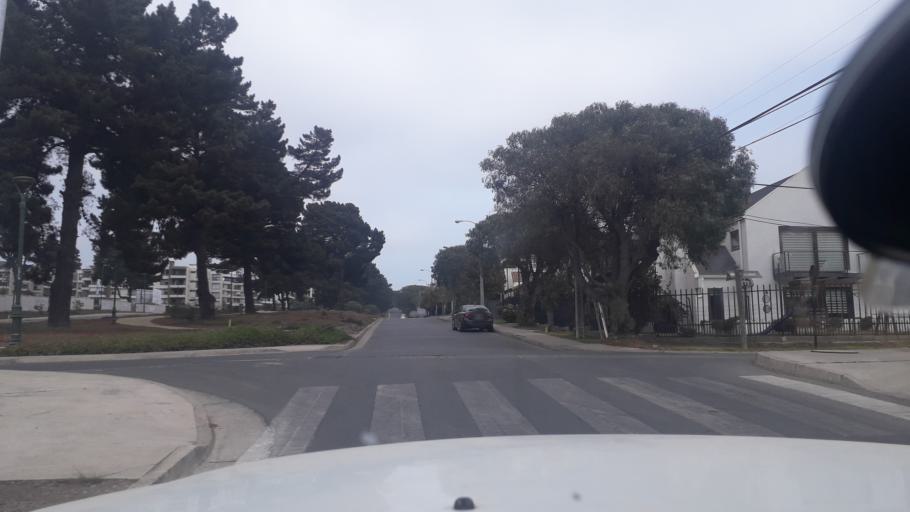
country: CL
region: Valparaiso
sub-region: Provincia de Valparaiso
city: Vina del Mar
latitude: -32.9390
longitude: -71.5372
